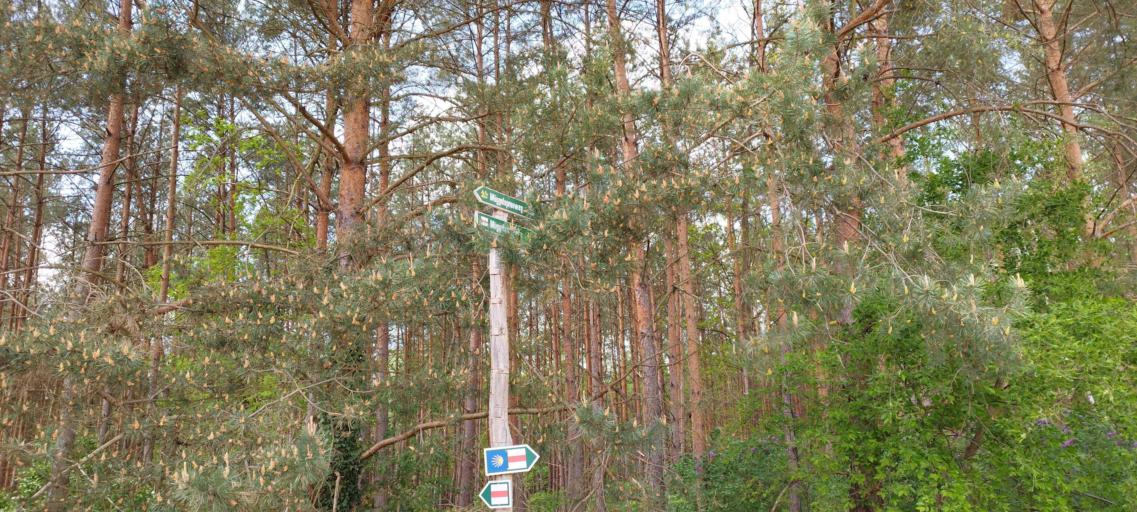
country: DE
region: Brandenburg
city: Spreenhagen
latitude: 52.3925
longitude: 13.8884
